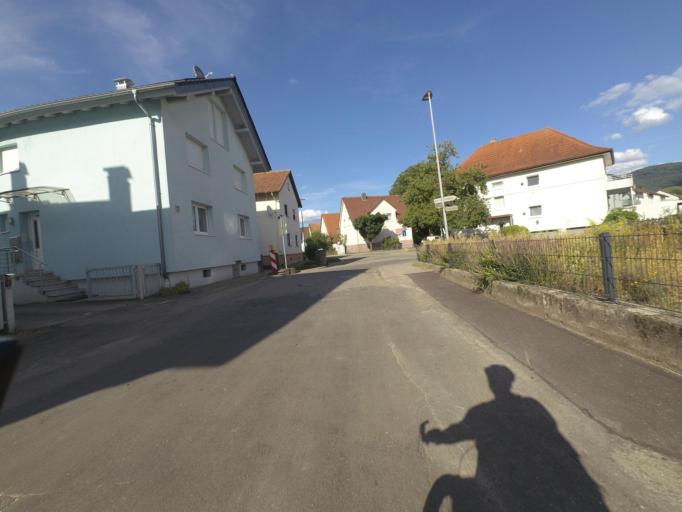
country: DE
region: Baden-Wuerttemberg
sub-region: Karlsruhe Region
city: Sinzheim
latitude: 48.7660
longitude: 8.1611
